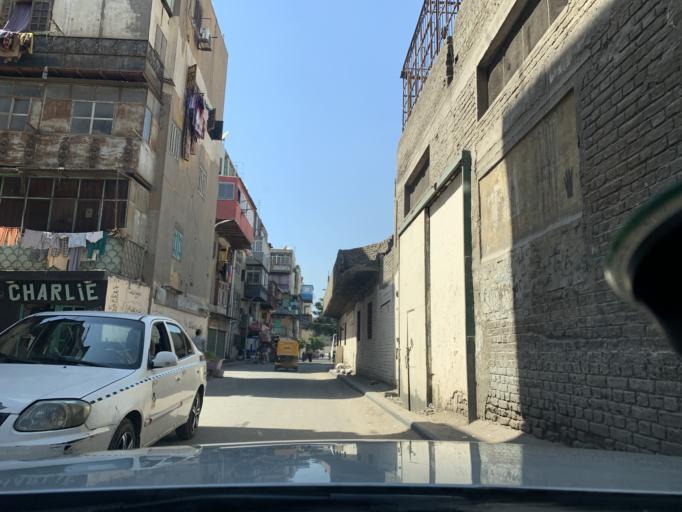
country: EG
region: Muhafazat al Qahirah
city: Cairo
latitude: 30.0766
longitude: 31.2582
